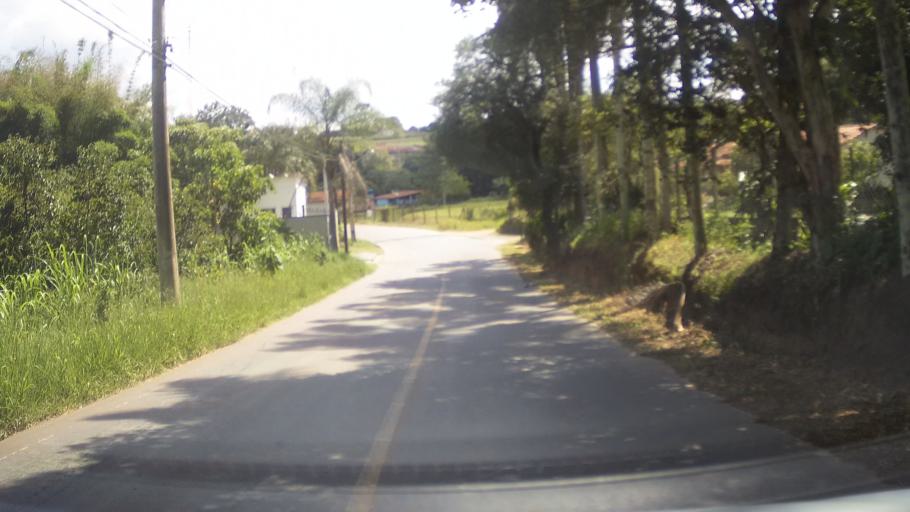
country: BR
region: Sao Paulo
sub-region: Varzea Paulista
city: Varzea Paulista
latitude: -23.1400
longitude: -46.8175
